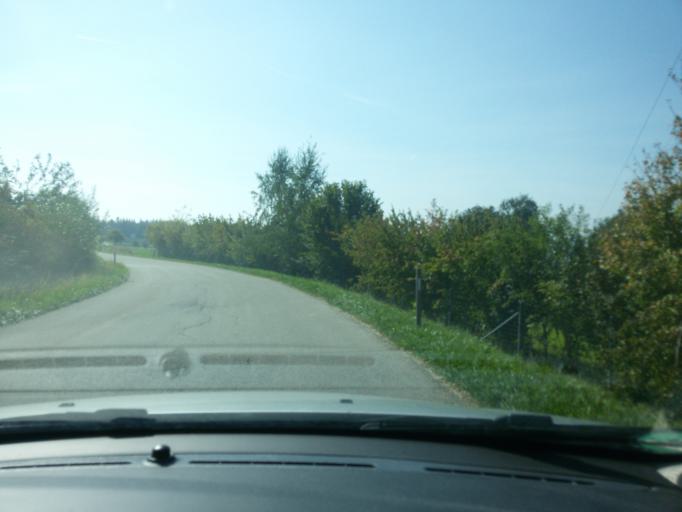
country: DE
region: Bavaria
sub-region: Swabia
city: Munster
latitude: 48.2128
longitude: 10.6101
